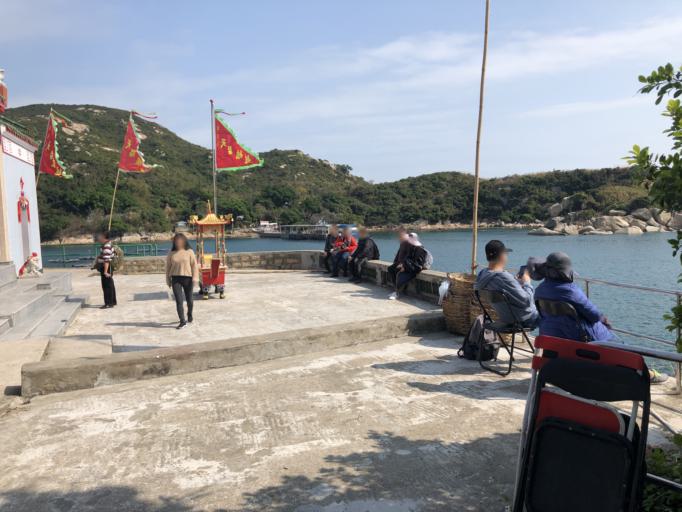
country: HK
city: Sok Kwu Wan
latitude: 22.1643
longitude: 114.2511
